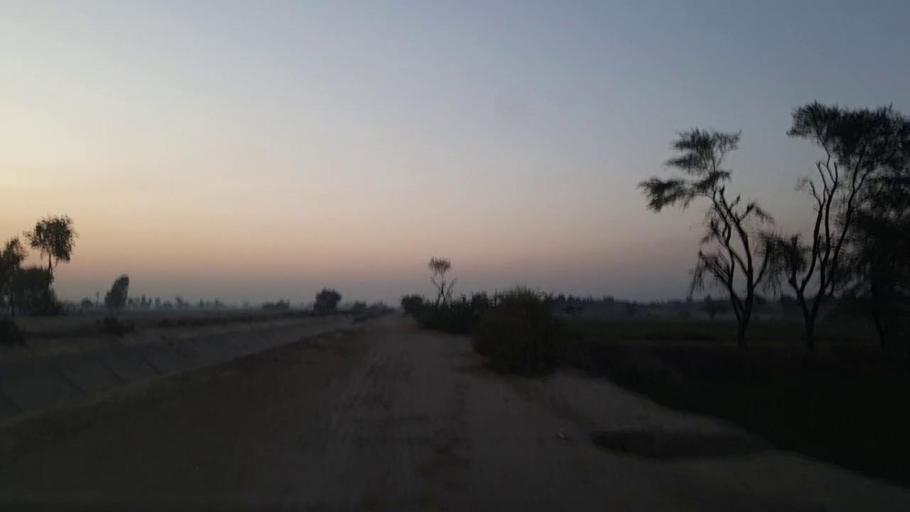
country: PK
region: Sindh
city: Daur
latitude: 26.4823
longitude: 68.4838
